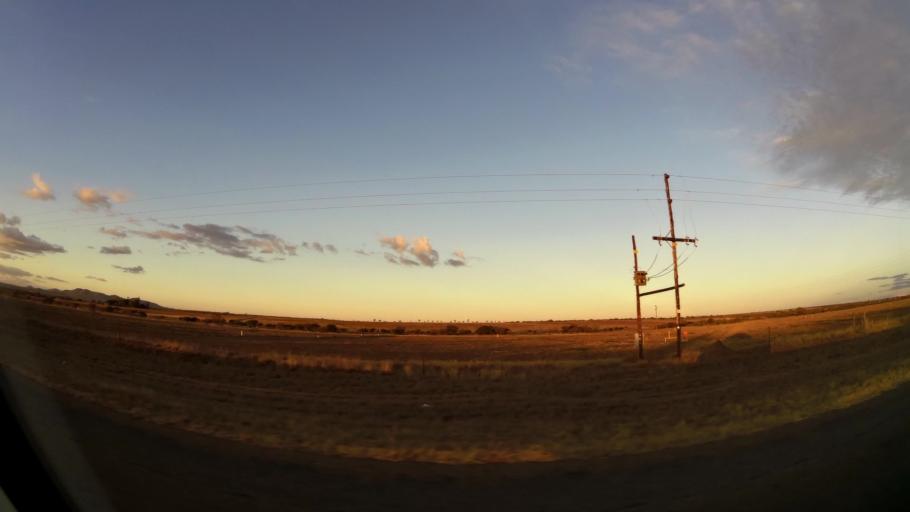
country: ZA
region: Limpopo
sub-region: Capricorn District Municipality
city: Polokwane
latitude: -23.7870
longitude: 29.4757
